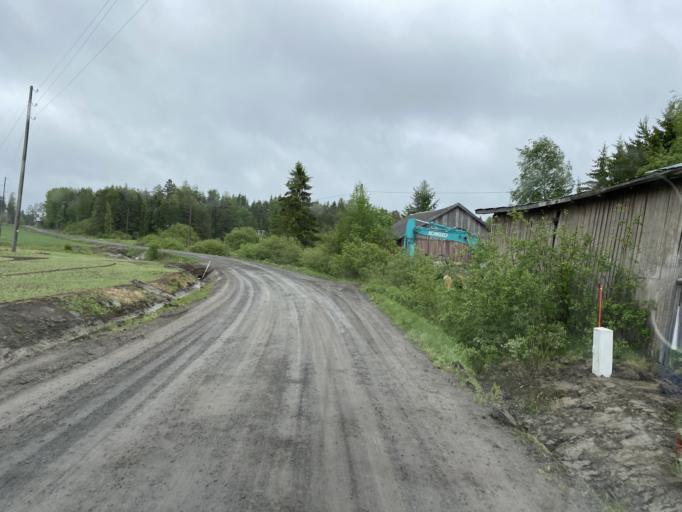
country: FI
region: Haeme
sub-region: Forssa
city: Forssa
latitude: 60.9374
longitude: 23.5844
